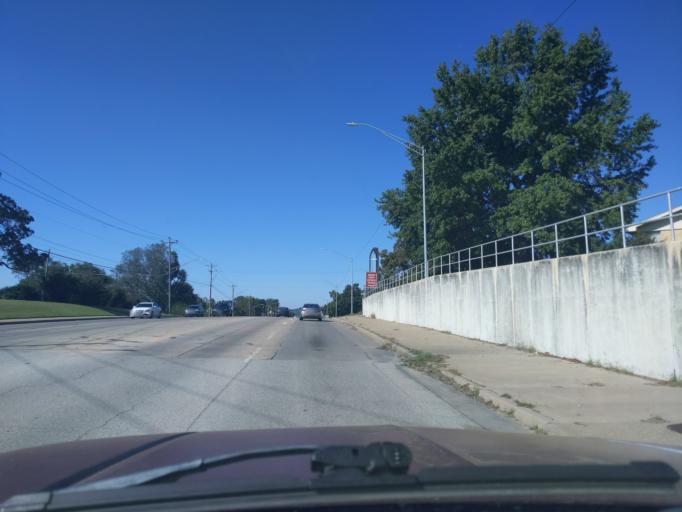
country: US
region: Oklahoma
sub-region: Creek County
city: Sapulpa
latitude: 35.9885
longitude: -96.0897
